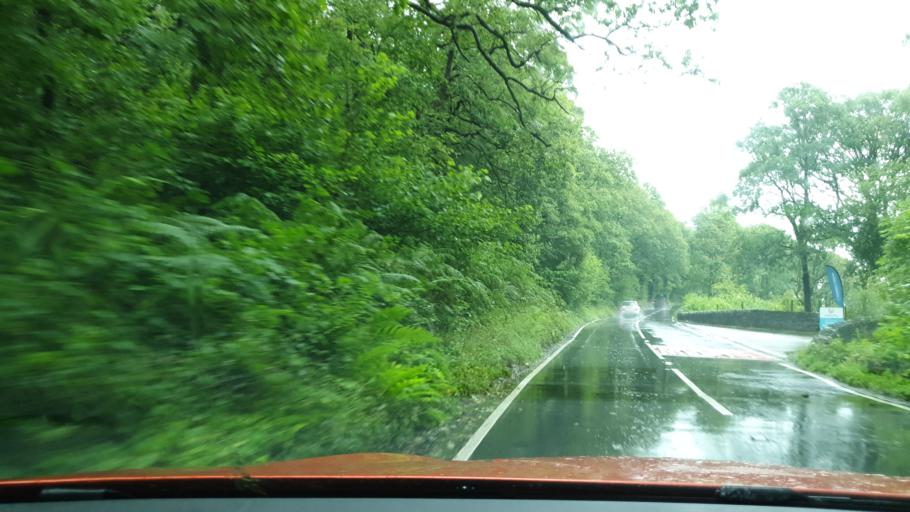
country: GB
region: England
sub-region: Cumbria
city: Ambleside
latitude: 54.3505
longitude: -3.0866
